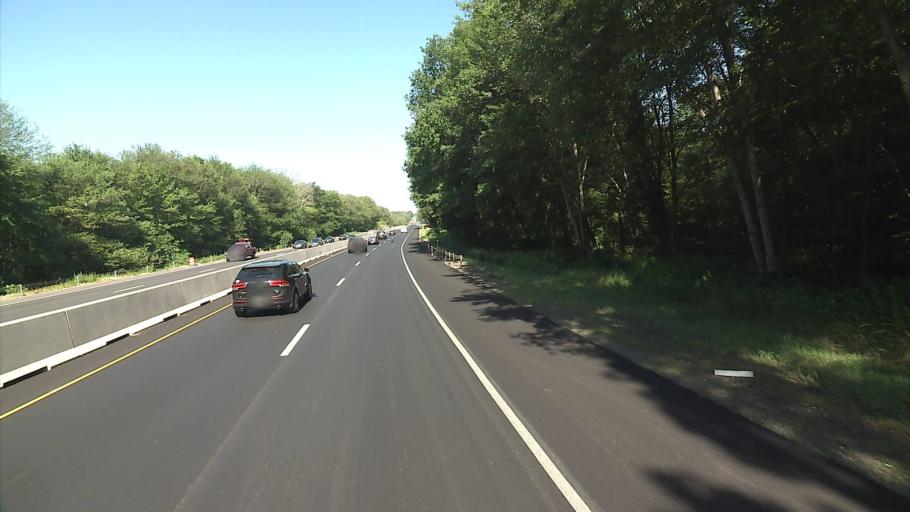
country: US
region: Connecticut
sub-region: Middlesex County
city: Old Saybrook Center
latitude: 41.3163
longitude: -72.2900
